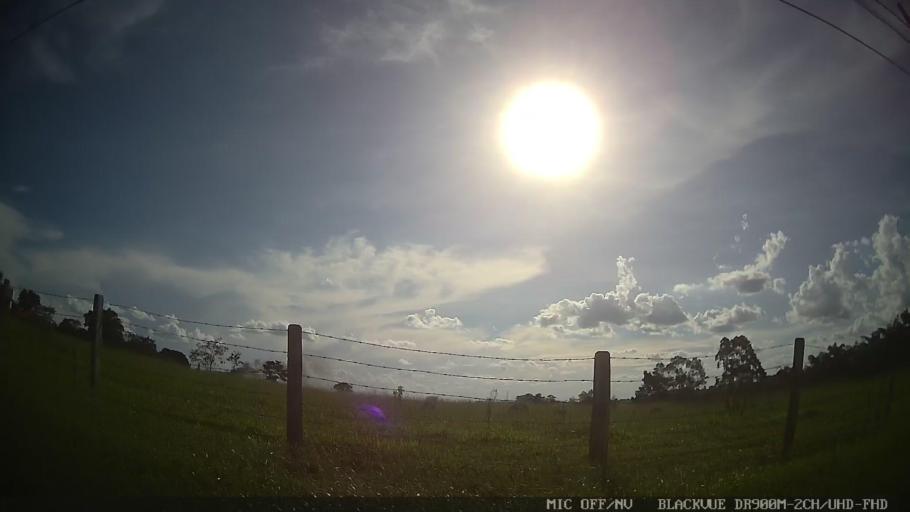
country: BR
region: Sao Paulo
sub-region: Tiete
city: Tiete
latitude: -23.0920
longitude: -47.7793
